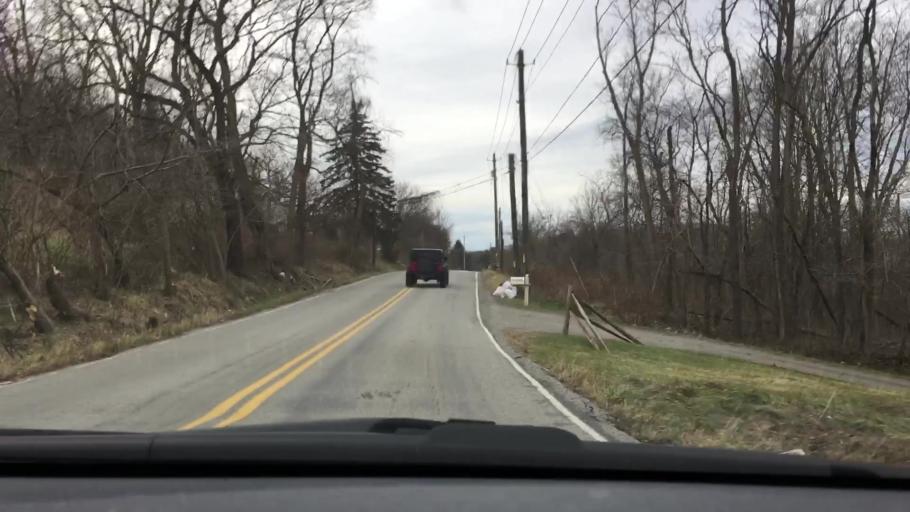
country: US
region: Pennsylvania
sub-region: Washington County
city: Midland
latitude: 40.2725
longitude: -80.2199
